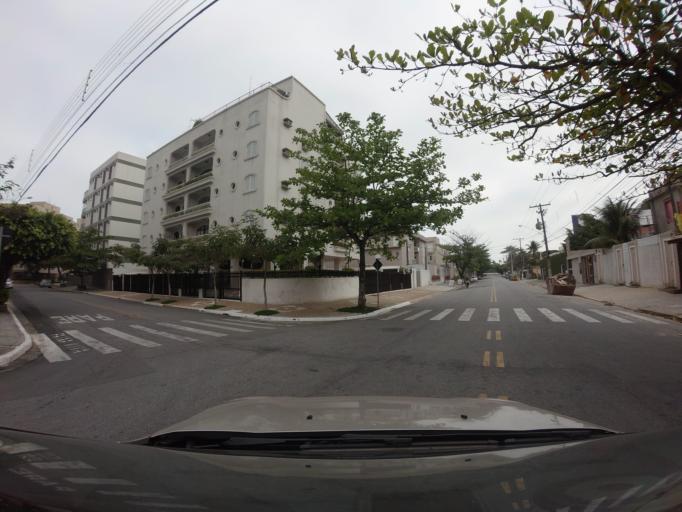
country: BR
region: Sao Paulo
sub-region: Guaruja
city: Guaruja
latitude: -23.9859
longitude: -46.2385
